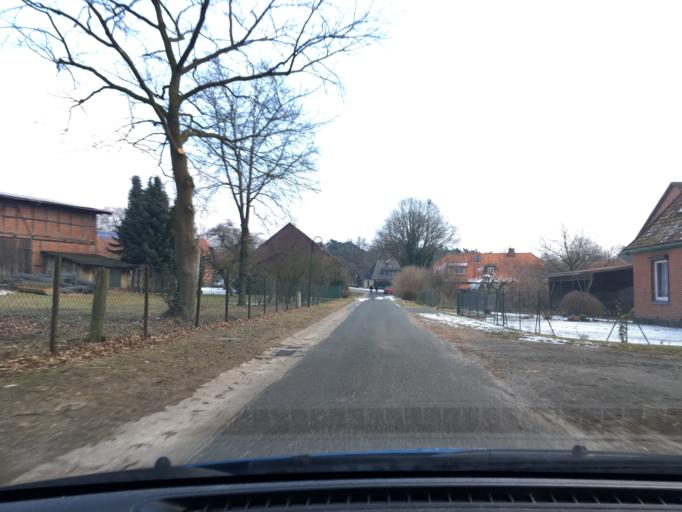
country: DE
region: Lower Saxony
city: Bienenbuttel
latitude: 53.1516
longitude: 10.4763
